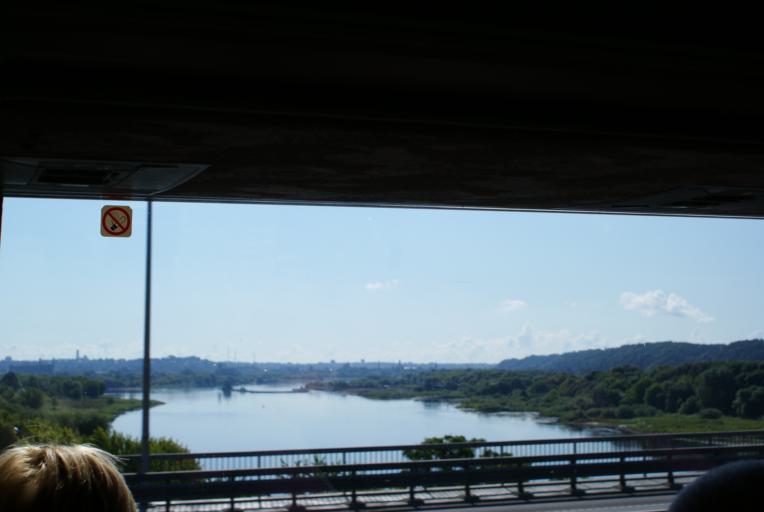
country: LT
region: Kauno apskritis
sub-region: Kauno rajonas
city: Akademija (Kaunas)
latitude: 54.9088
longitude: 23.8337
